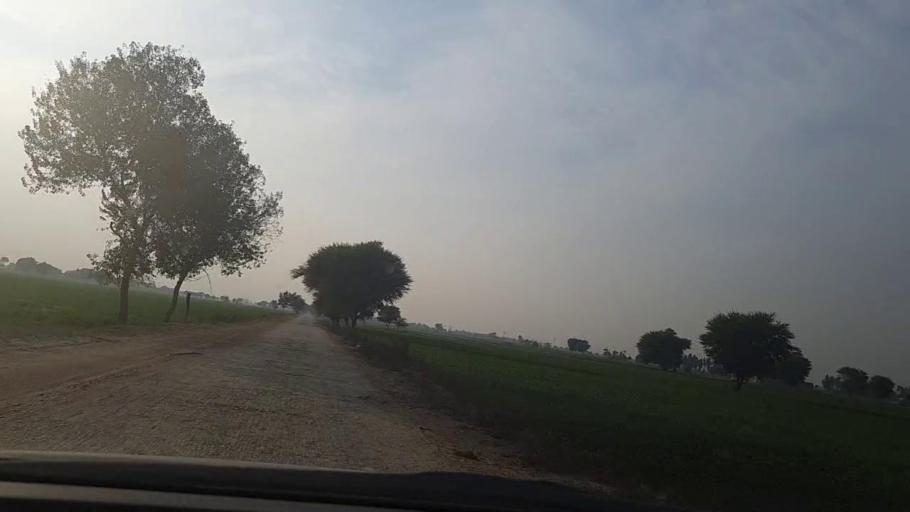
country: PK
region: Sindh
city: Daulatpur
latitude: 26.3369
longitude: 68.0360
